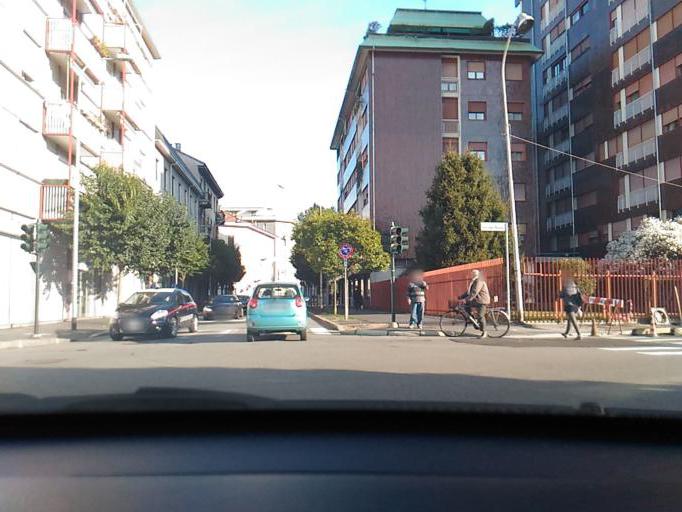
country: IT
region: Lombardy
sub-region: Provincia di Varese
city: Busto Arsizio
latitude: 45.6094
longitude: 8.8501
